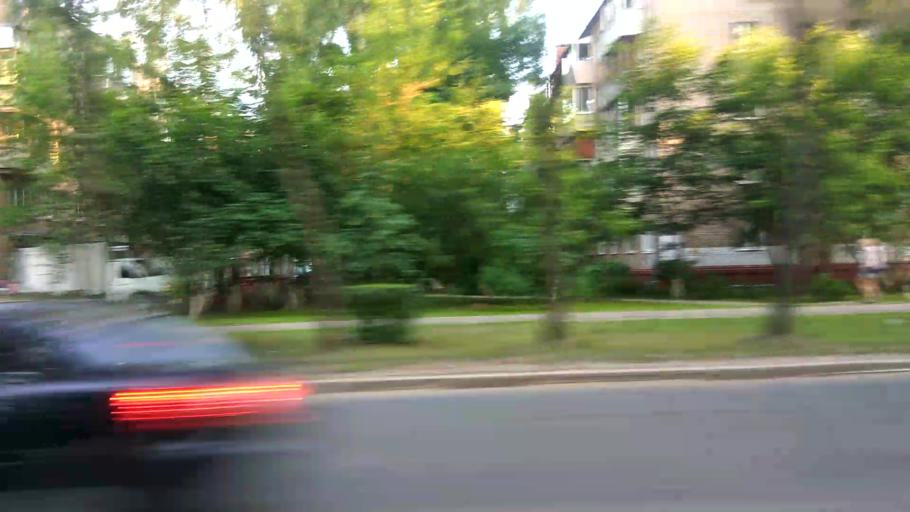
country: RU
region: Moskovskaya
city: Korolev
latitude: 55.9135
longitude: 37.8182
